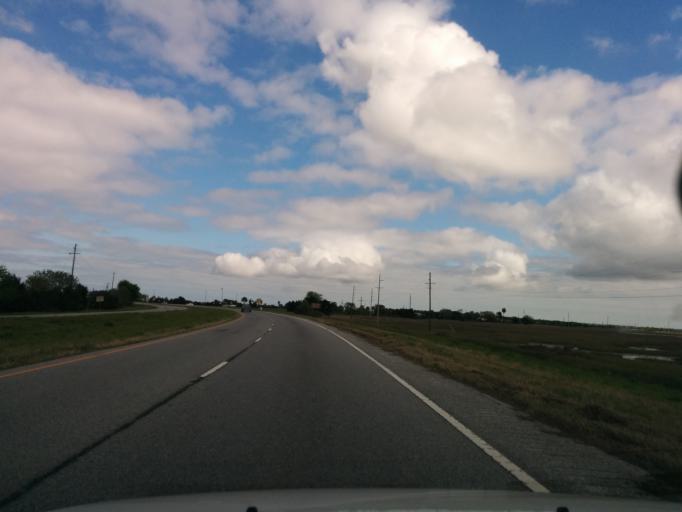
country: US
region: Georgia
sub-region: Glynn County
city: Brunswick
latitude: 31.1051
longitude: -81.4975
